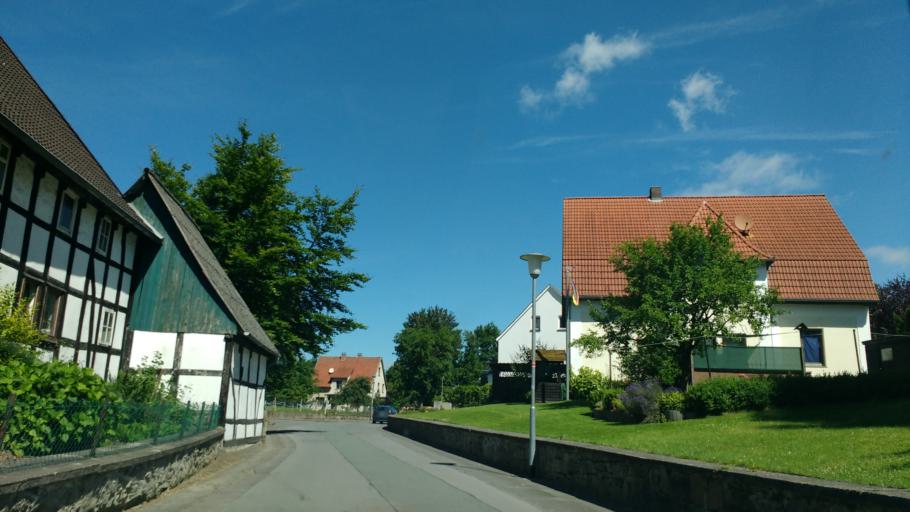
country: DE
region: North Rhine-Westphalia
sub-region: Regierungsbezirk Detmold
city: Dorentrup
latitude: 52.0242
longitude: 9.0550
